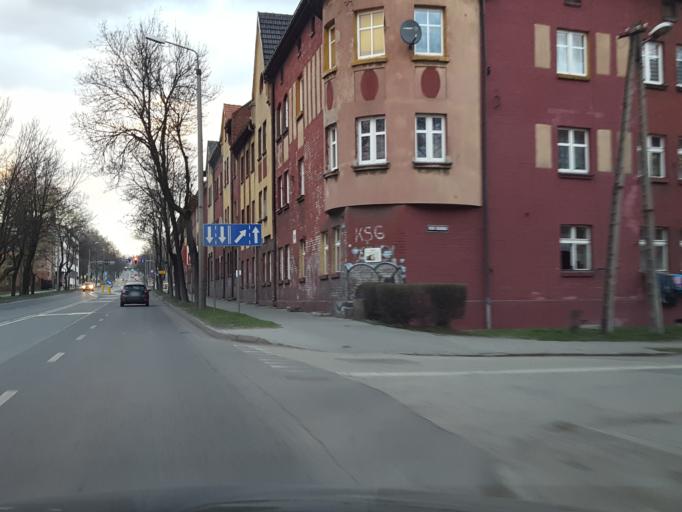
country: PL
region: Silesian Voivodeship
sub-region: Ruda Slaska
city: Ruda Slaska
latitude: 50.2682
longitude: 18.8625
